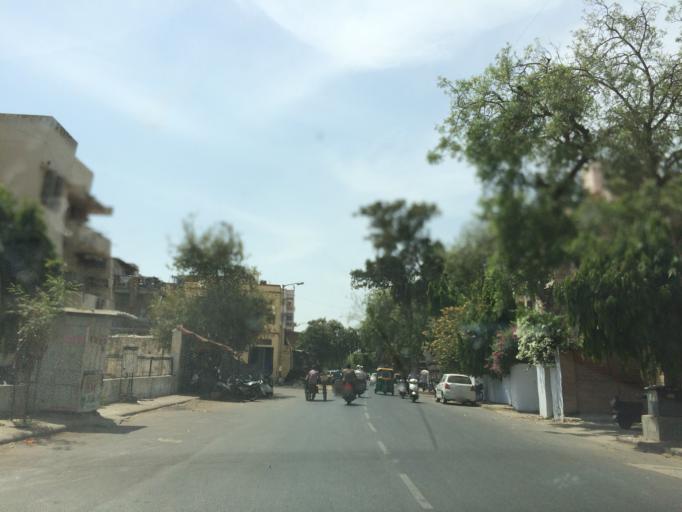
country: IN
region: Gujarat
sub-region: Ahmadabad
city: Ahmedabad
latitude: 23.0098
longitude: 72.5566
